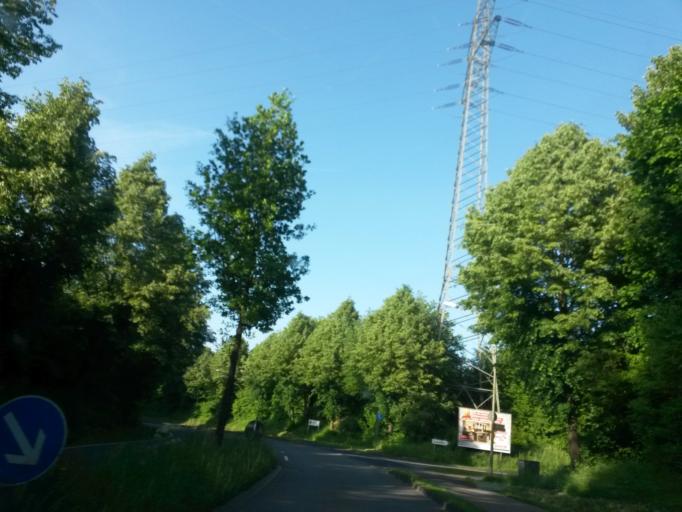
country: DE
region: North Rhine-Westphalia
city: Bergneustadt
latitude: 51.0166
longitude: 7.6548
